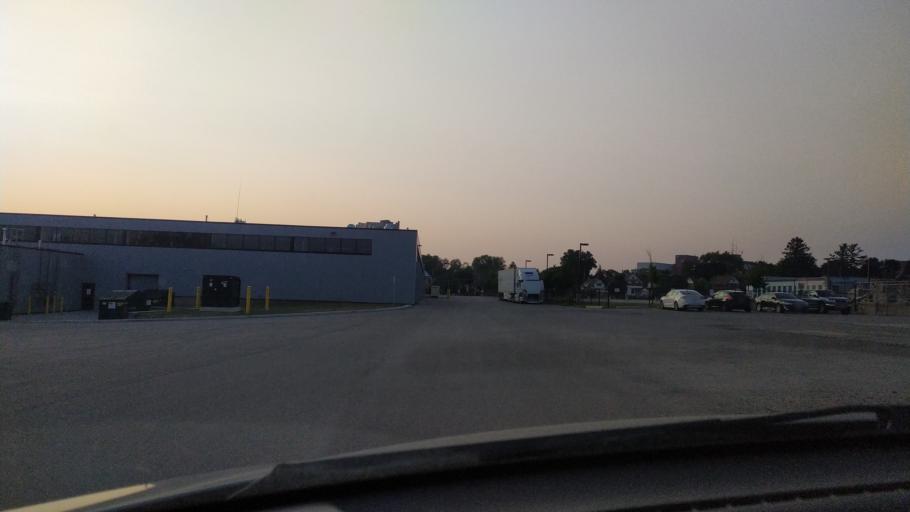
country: CA
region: Ontario
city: Waterloo
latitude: 43.4513
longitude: -80.5122
